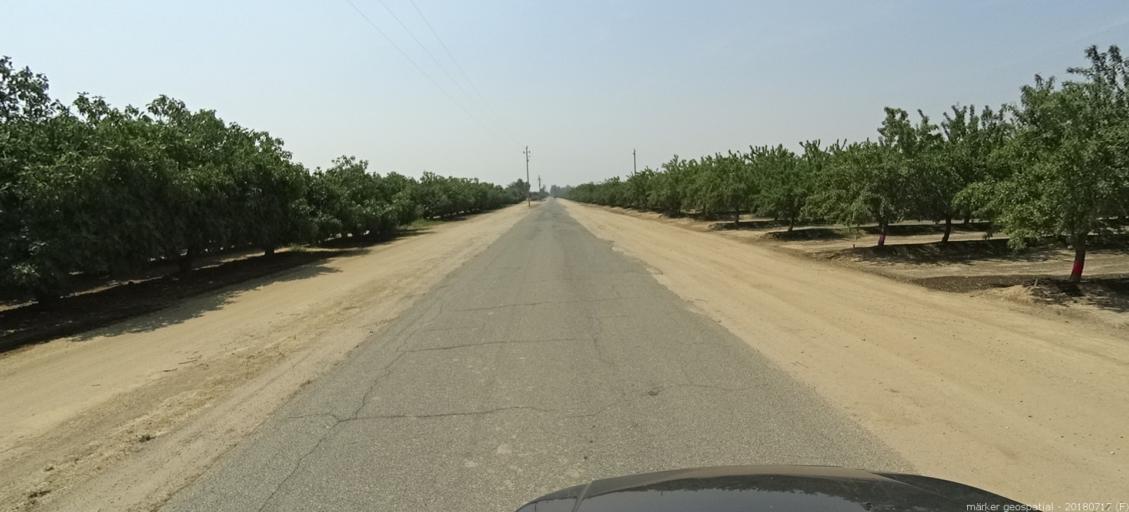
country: US
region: California
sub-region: Madera County
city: Fairmead
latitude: 37.1402
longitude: -120.1382
